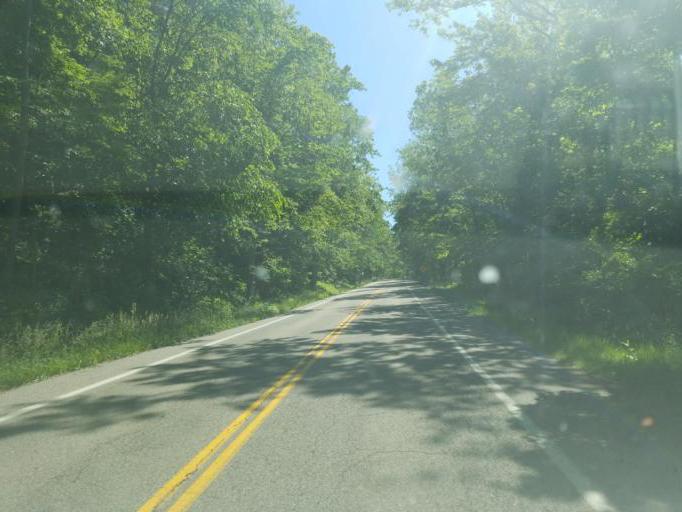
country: US
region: Ohio
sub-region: Summit County
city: Peninsula
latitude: 41.2194
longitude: -81.5228
